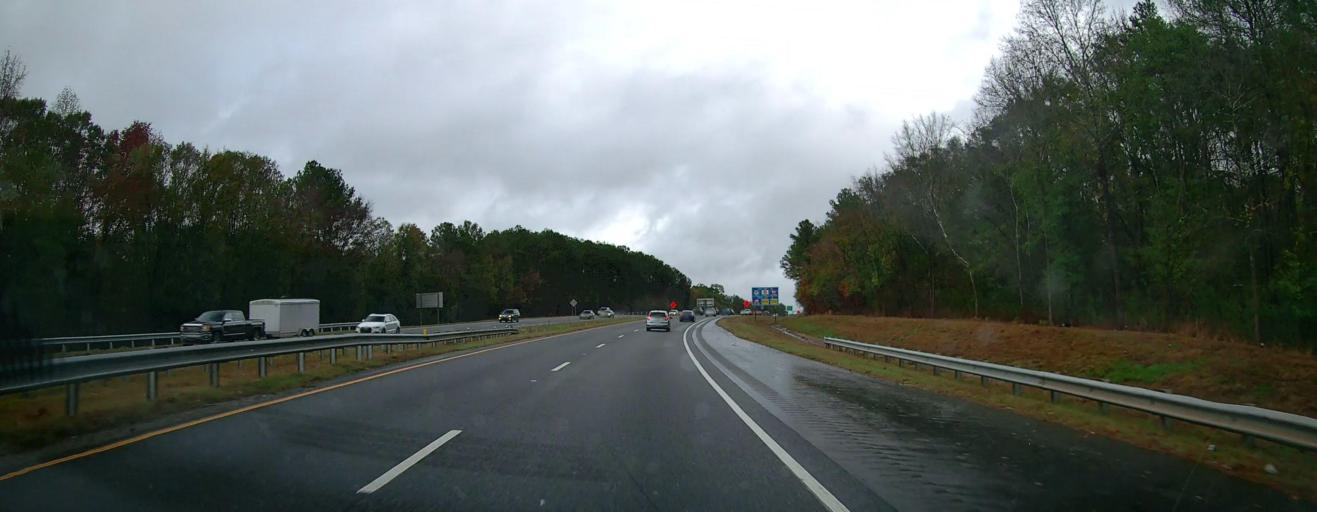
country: US
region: Georgia
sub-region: Clarke County
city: Athens
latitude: 33.9402
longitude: -83.3643
